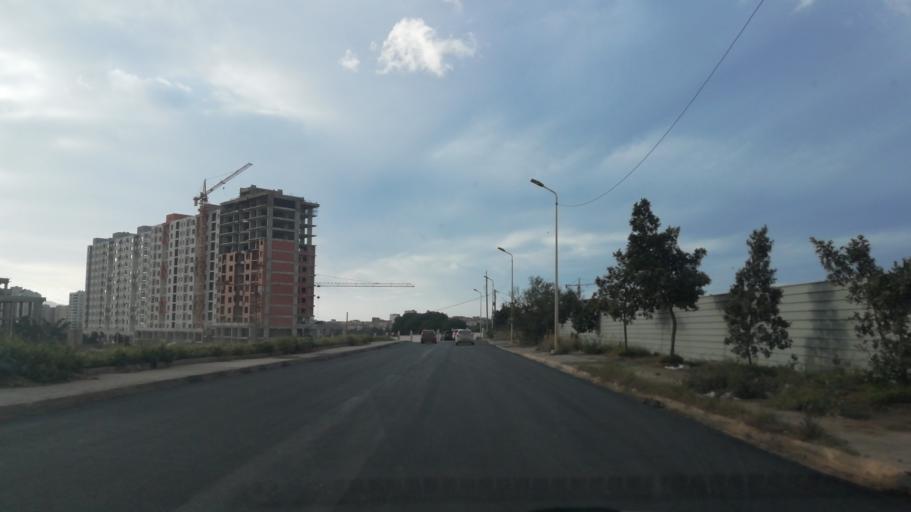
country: DZ
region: Oran
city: Bir el Djir
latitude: 35.7121
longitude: -0.5709
